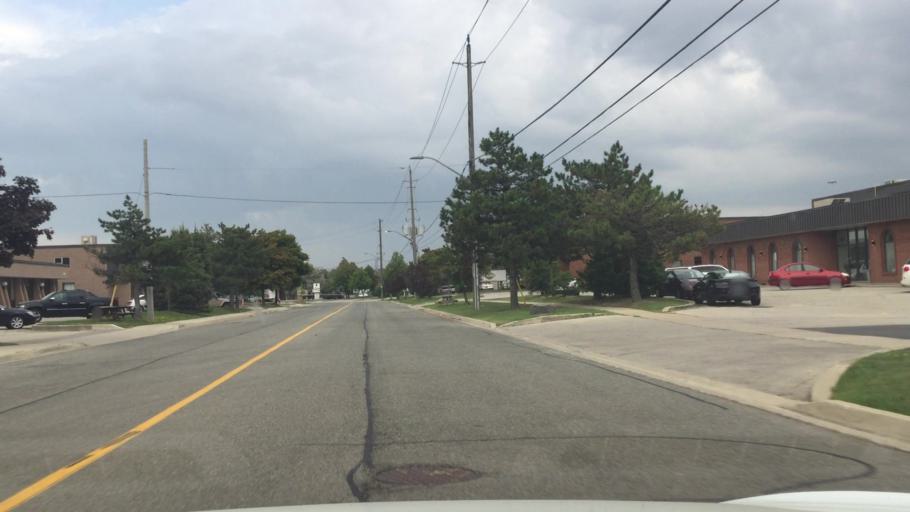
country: CA
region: Ontario
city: Mississauga
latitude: 43.6266
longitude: -79.6390
